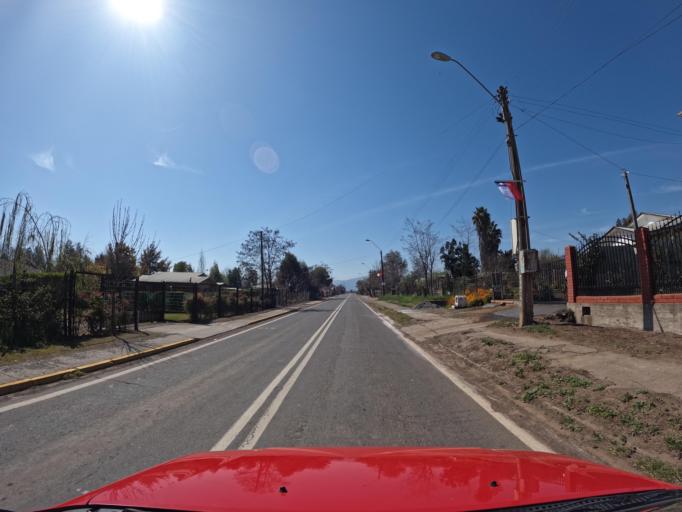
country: CL
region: Maule
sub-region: Provincia de Curico
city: Molina
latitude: -35.0560
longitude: -71.4872
